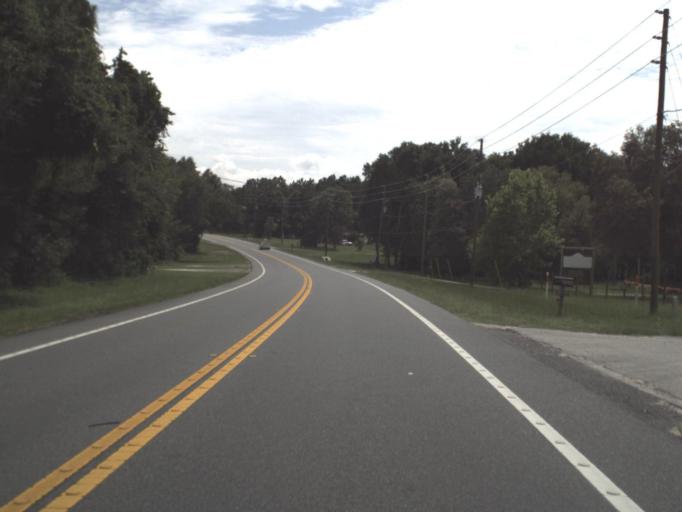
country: US
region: Florida
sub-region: Citrus County
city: Hernando
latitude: 28.9631
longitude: -82.3756
